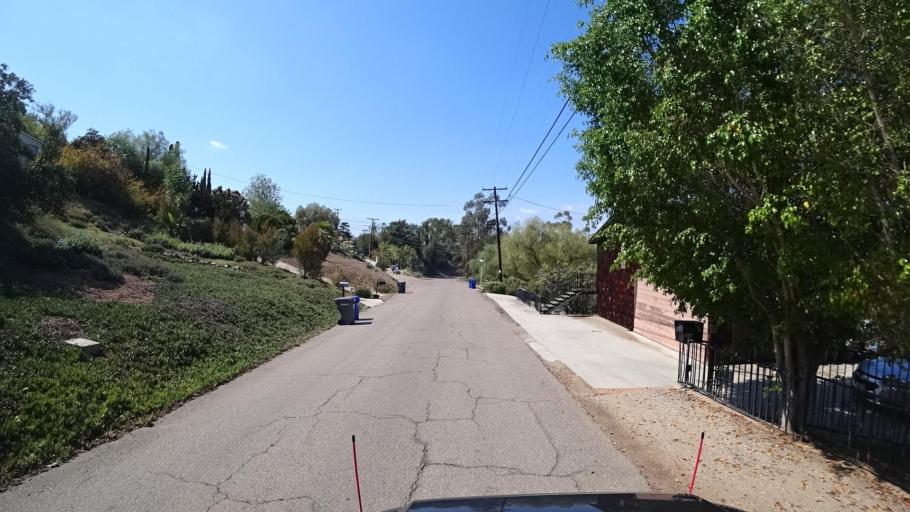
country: US
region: California
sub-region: San Diego County
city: Spring Valley
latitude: 32.7375
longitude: -116.9967
